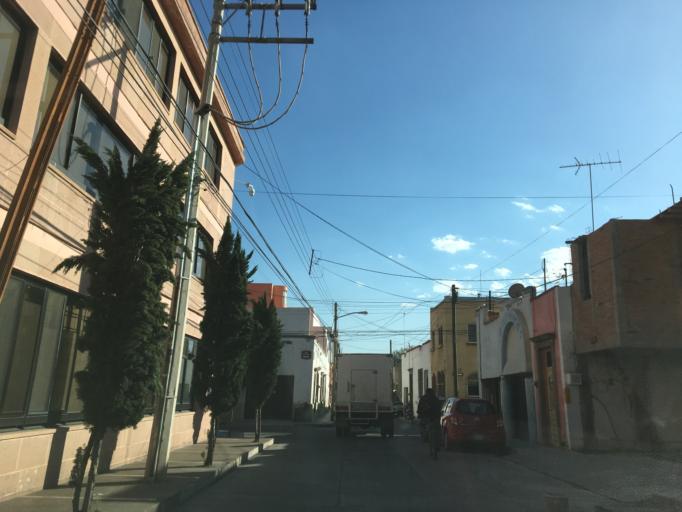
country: MX
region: San Luis Potosi
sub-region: San Luis Potosi
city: San Luis Potosi
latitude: 22.1487
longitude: -100.9928
